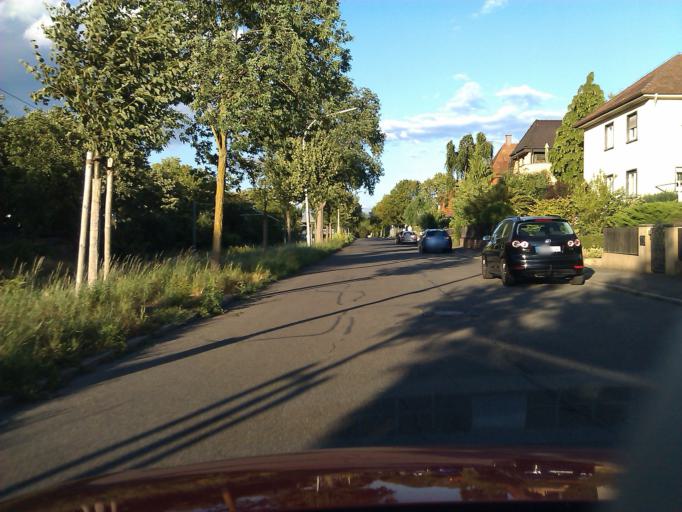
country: DE
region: Baden-Wuerttemberg
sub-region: Regierungsbezirk Stuttgart
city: Heilbronn
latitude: 49.1398
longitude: 9.1770
